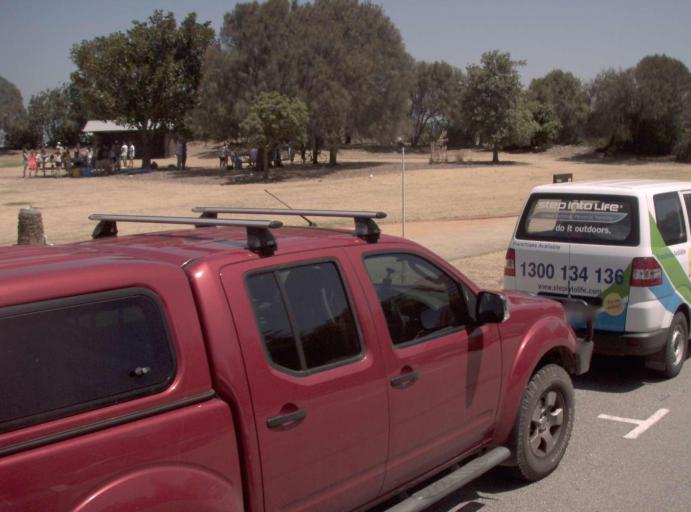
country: AU
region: Victoria
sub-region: Port Phillip
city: St Kilda West
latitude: -37.8591
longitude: 144.9702
